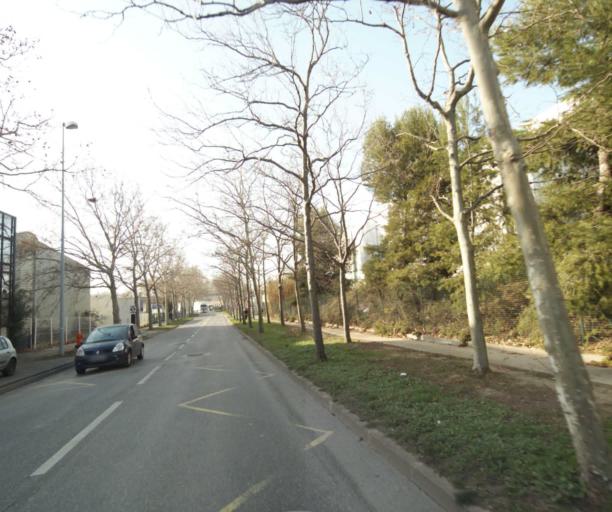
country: FR
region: Provence-Alpes-Cote d'Azur
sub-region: Departement des Bouches-du-Rhone
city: Saint-Victoret
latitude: 43.4226
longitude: 5.2618
